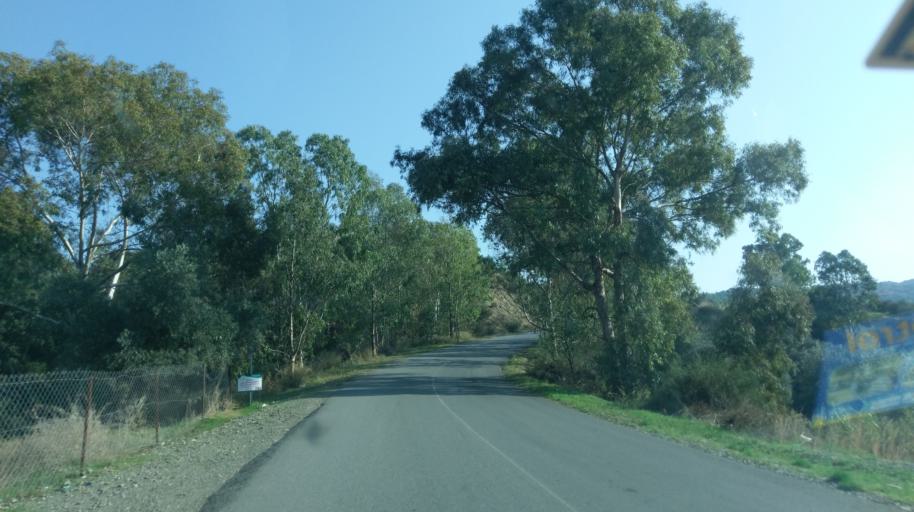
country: CY
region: Lefkosia
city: Kato Pyrgos
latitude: 35.1647
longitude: 32.7487
